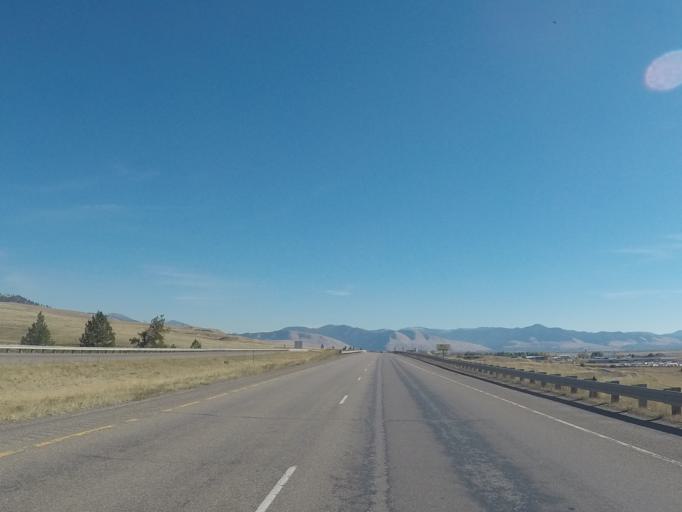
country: US
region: Montana
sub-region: Missoula County
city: Orchard Homes
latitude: 46.9466
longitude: -114.1232
